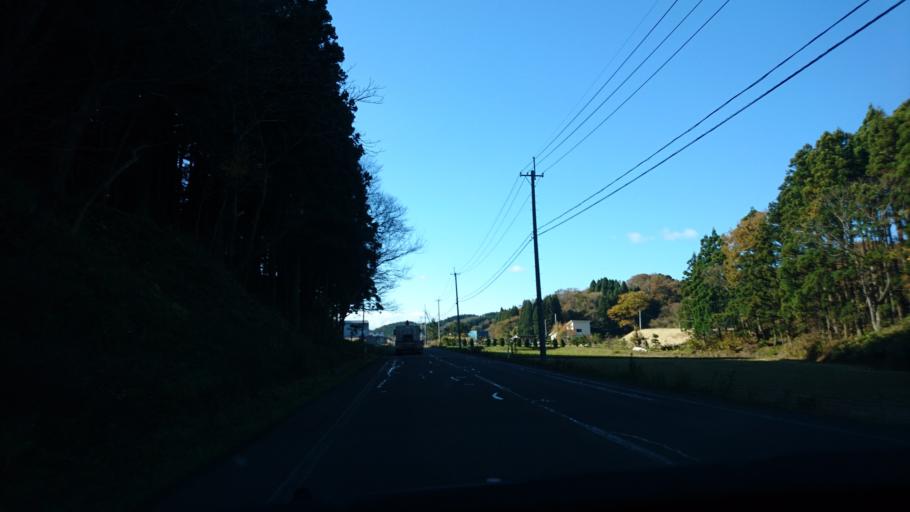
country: JP
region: Akita
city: Akita
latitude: 39.3522
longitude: 140.1012
